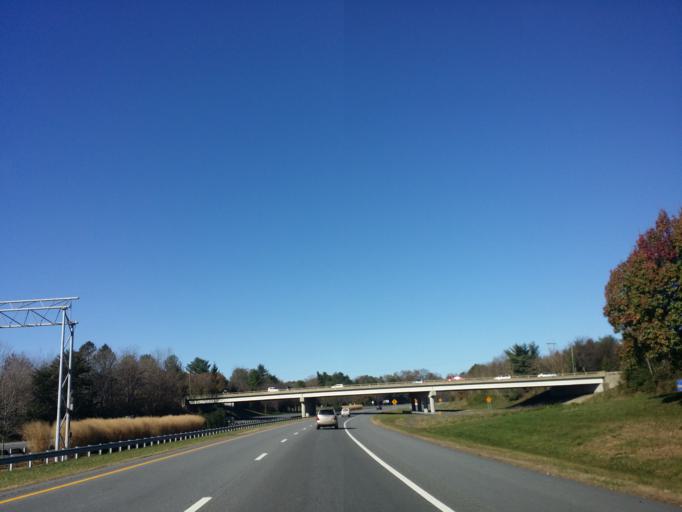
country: US
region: North Carolina
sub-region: Buncombe County
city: Biltmore Forest
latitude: 35.5675
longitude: -82.5053
